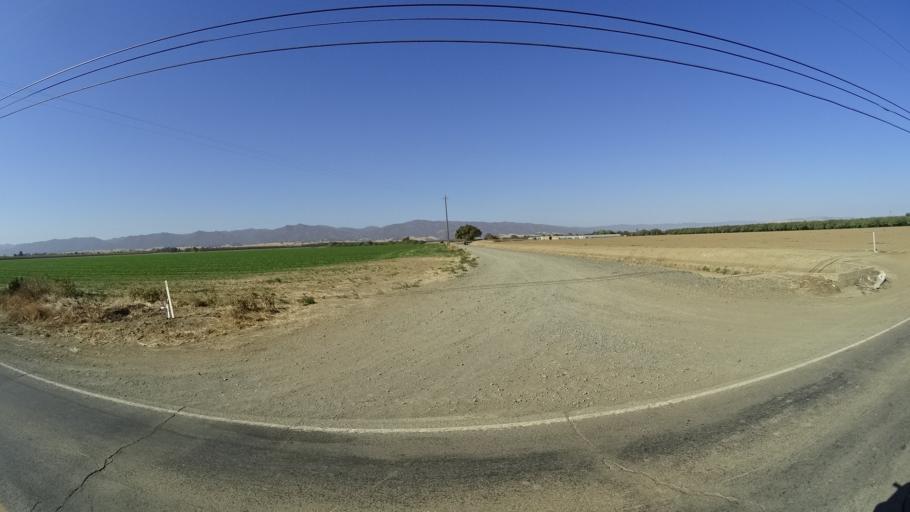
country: US
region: California
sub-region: Yolo County
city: Cottonwood
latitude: 38.6471
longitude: -121.9712
